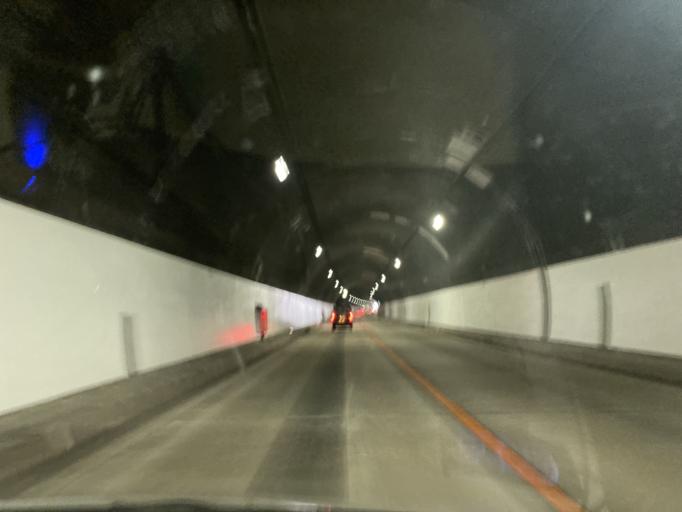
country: JP
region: Wakayama
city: Iwade
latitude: 34.3519
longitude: 135.2901
